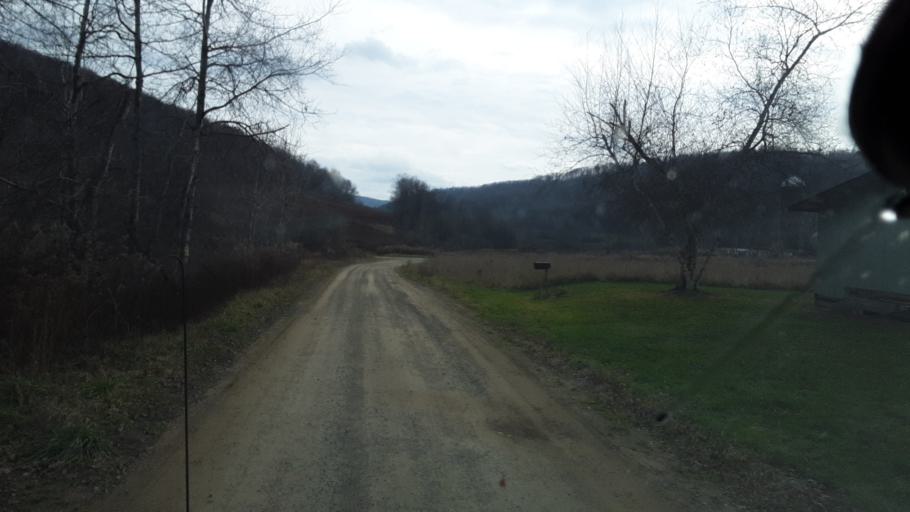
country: US
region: Pennsylvania
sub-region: Tioga County
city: Westfield
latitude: 41.9038
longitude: -77.7148
